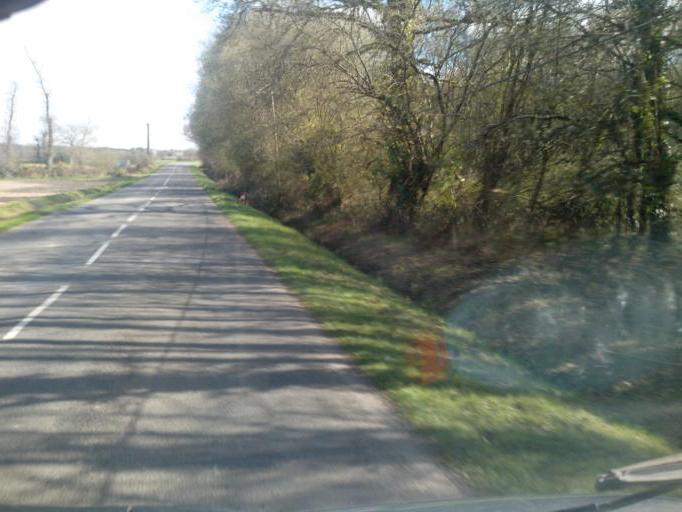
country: FR
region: Brittany
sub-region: Departement d'Ille-et-Vilaine
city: Paimpont
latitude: 48.0647
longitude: -2.1875
